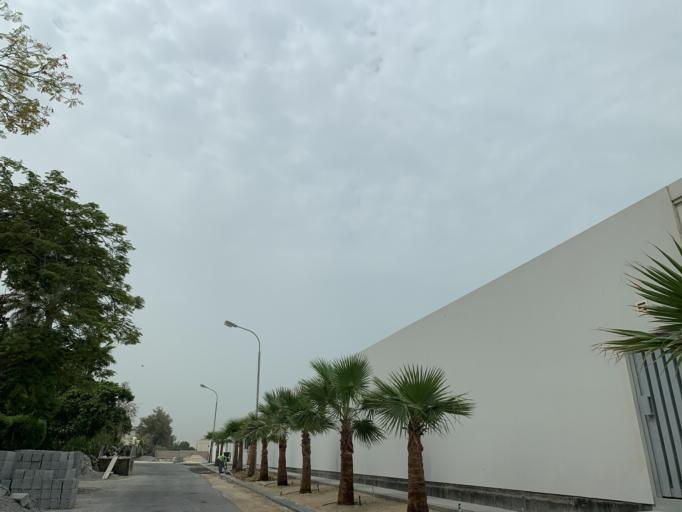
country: BH
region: Central Governorate
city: Madinat Hamad
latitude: 26.1790
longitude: 50.4698
